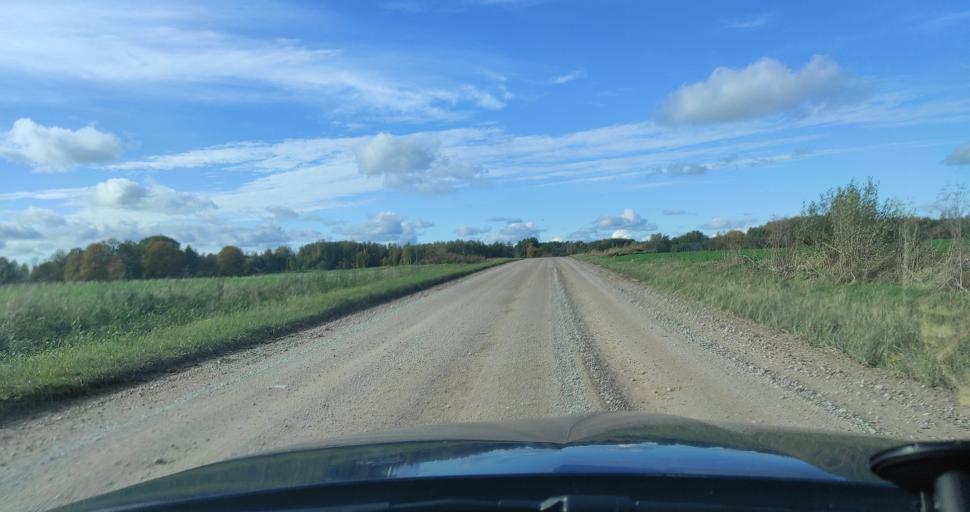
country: LV
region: Jaunpils
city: Jaunpils
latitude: 56.8306
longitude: 22.9889
